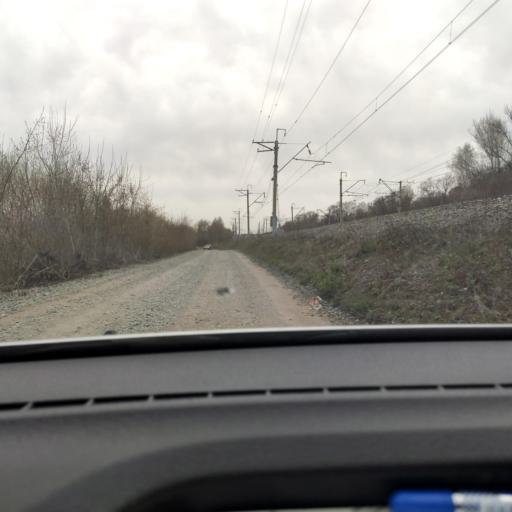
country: RU
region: Bashkortostan
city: Avdon
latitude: 54.6214
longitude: 55.6007
